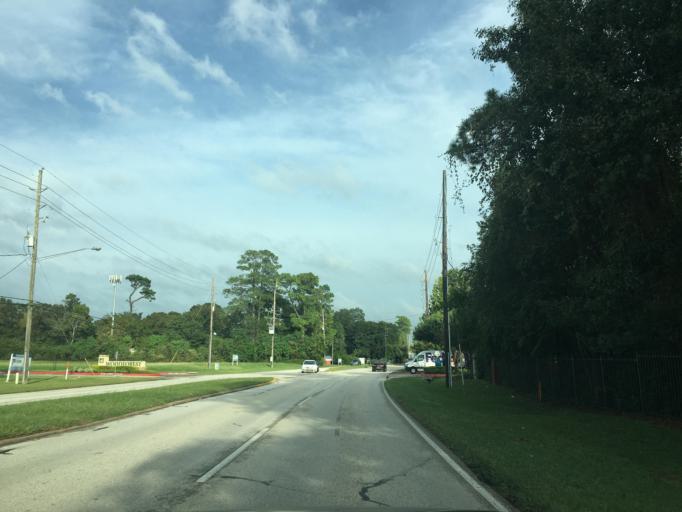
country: US
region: Texas
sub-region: Montgomery County
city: Oak Ridge North
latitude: 30.1267
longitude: -95.4620
